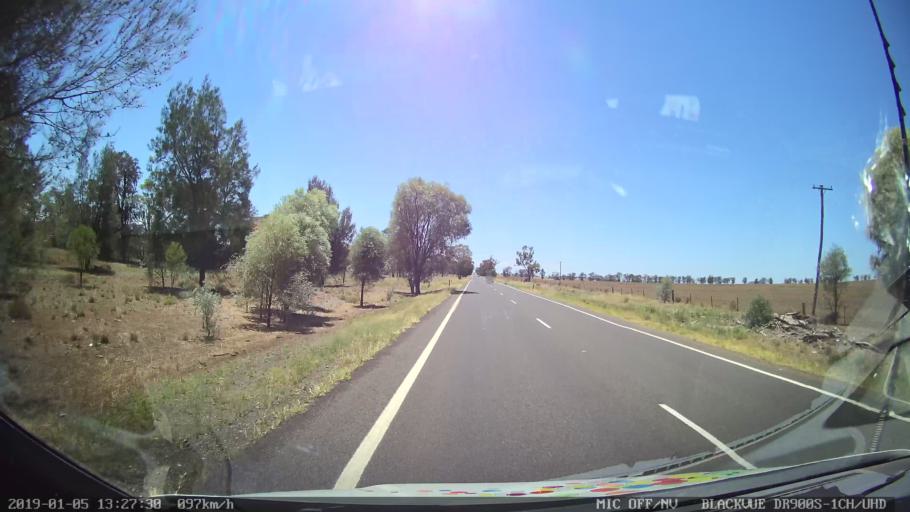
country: AU
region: New South Wales
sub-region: Gunnedah
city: Gunnedah
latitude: -31.0440
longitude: 150.0302
